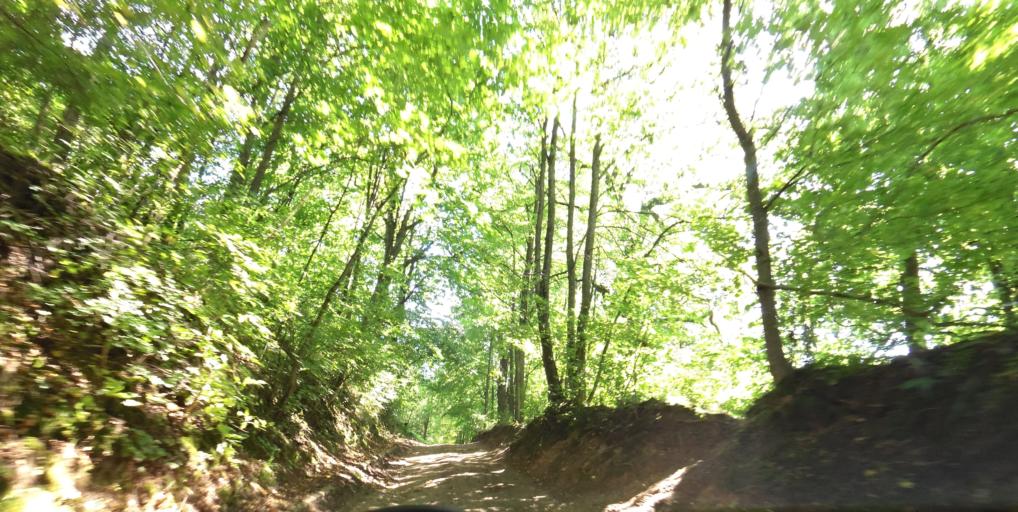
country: LT
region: Vilnius County
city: Rasos
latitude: 54.6844
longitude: 25.3606
